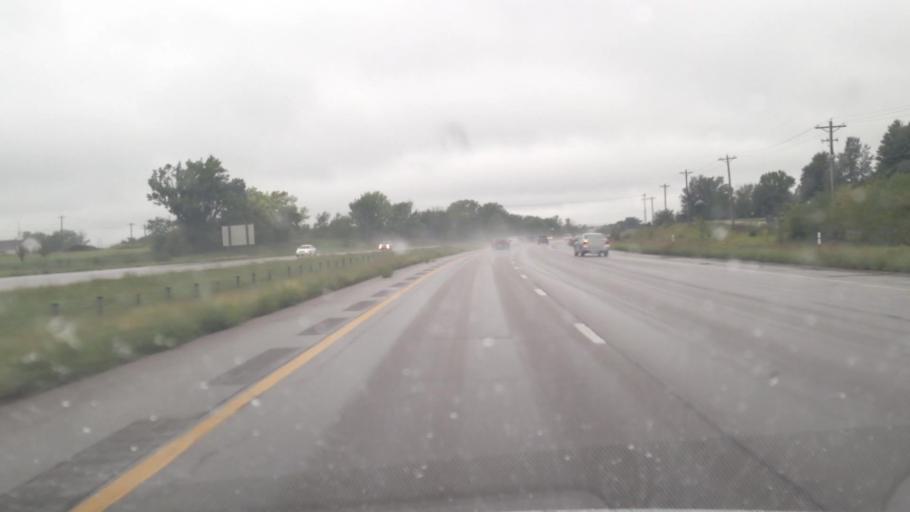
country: US
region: Kansas
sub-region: Douglas County
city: Eudora
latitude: 38.9296
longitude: -95.0992
